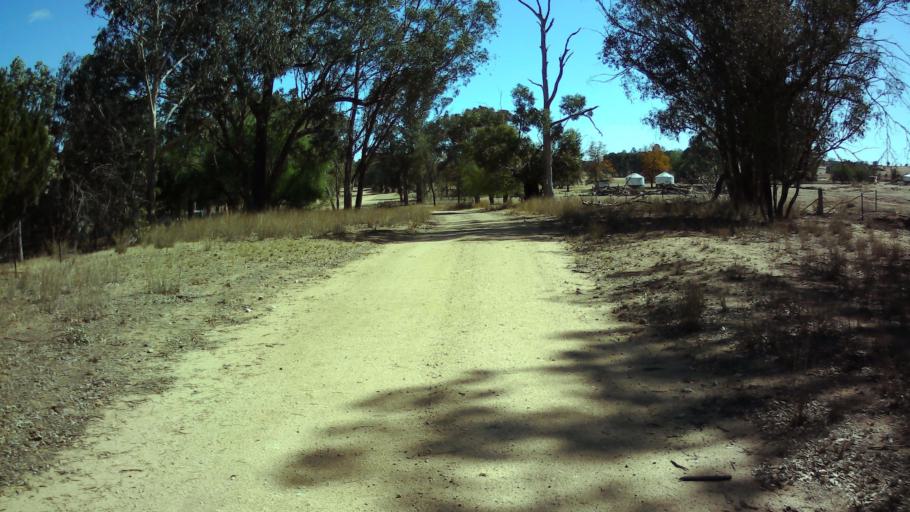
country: AU
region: New South Wales
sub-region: Weddin
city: Grenfell
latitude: -34.0079
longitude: 148.4352
